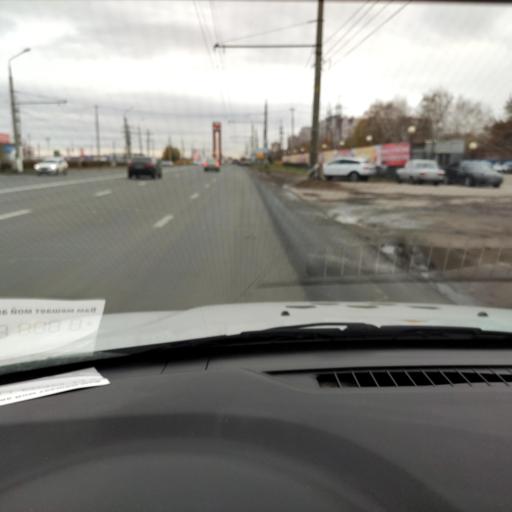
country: RU
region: Samara
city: Tol'yatti
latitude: 53.5509
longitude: 49.3147
